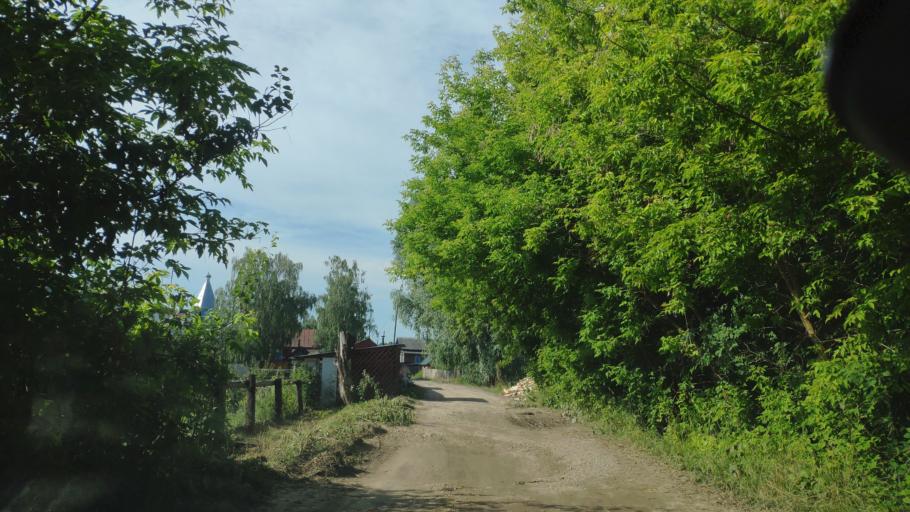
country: RU
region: Nizjnij Novgorod
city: Vorotynets
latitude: 56.1905
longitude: 45.7849
